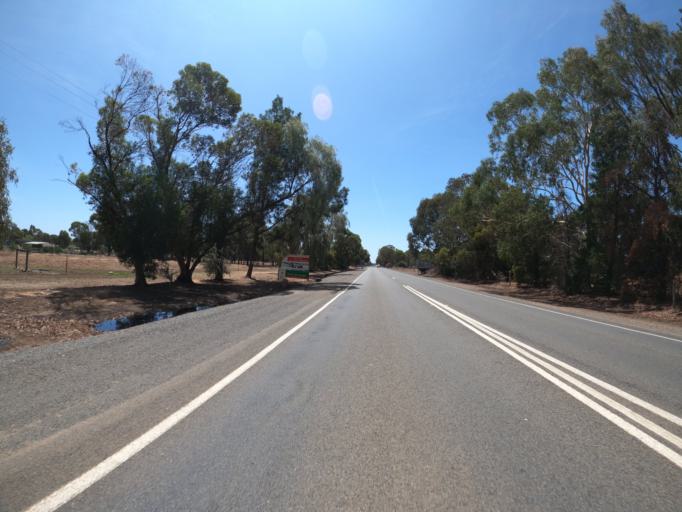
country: AU
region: Victoria
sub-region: Moira
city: Yarrawonga
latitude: -36.0395
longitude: 145.9954
